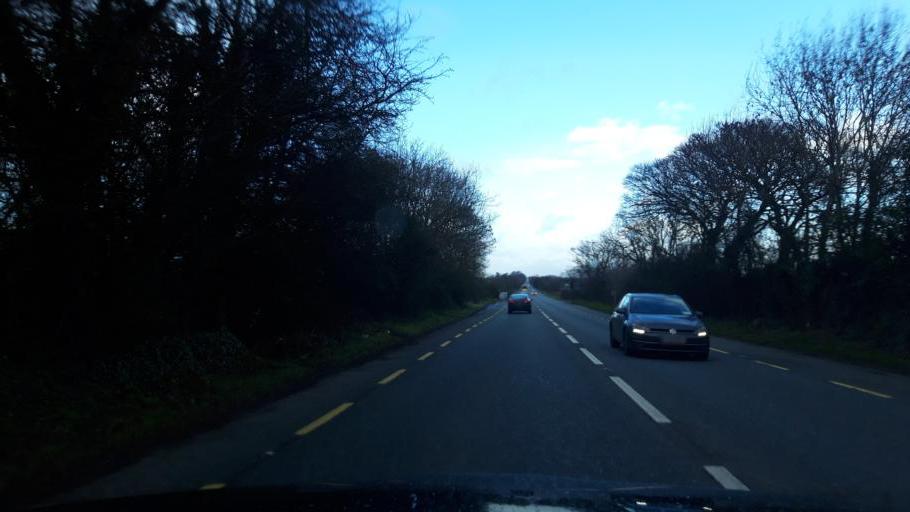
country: IE
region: Leinster
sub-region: An Mhi
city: Ashbourne
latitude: 53.5338
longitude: -6.4222
